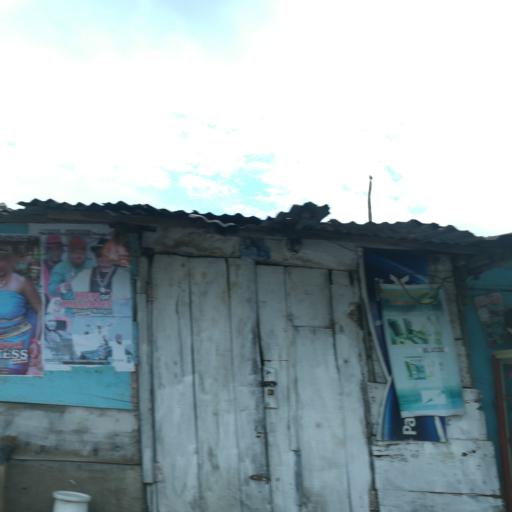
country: NG
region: Rivers
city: Port Harcourt
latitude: 4.7932
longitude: 7.0249
